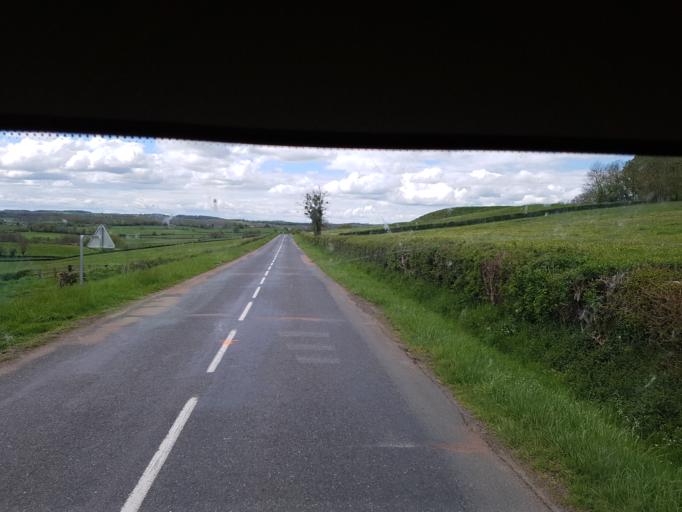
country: FR
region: Bourgogne
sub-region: Departement de Saone-et-Loire
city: Perrecy-les-Forges
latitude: 46.6050
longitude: 4.2233
